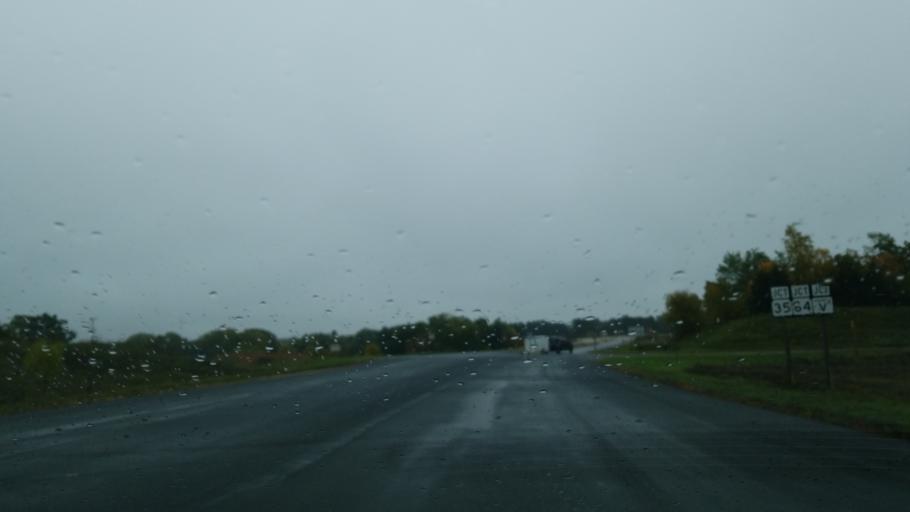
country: US
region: Minnesota
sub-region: Washington County
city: Stillwater
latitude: 45.0905
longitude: -92.7442
